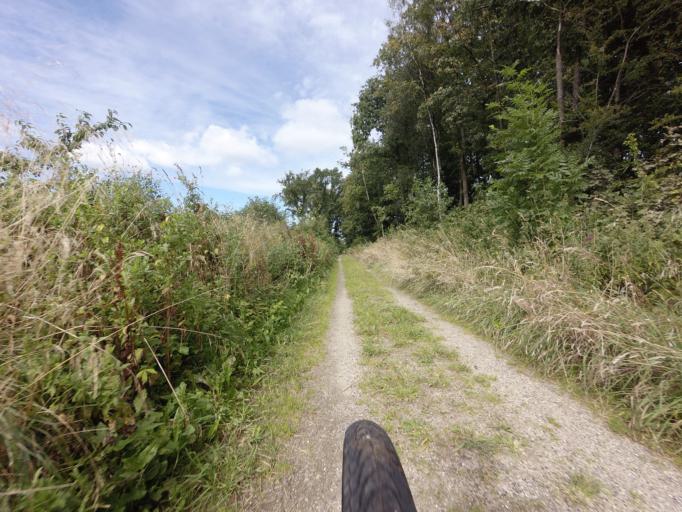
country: DK
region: Central Jutland
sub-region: Syddjurs Kommune
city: Ryomgard
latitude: 56.3858
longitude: 10.5335
